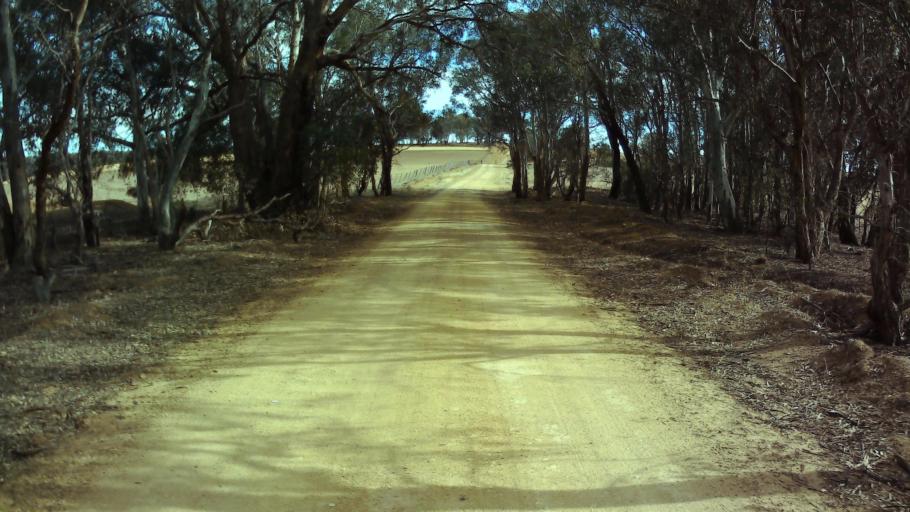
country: AU
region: New South Wales
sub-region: Weddin
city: Grenfell
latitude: -33.8983
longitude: 148.2035
